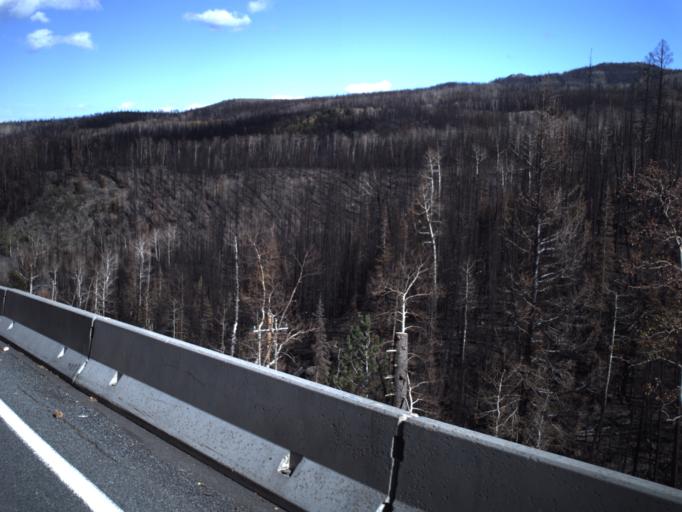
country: US
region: Utah
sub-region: Iron County
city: Parowan
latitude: 37.7123
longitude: -112.8506
